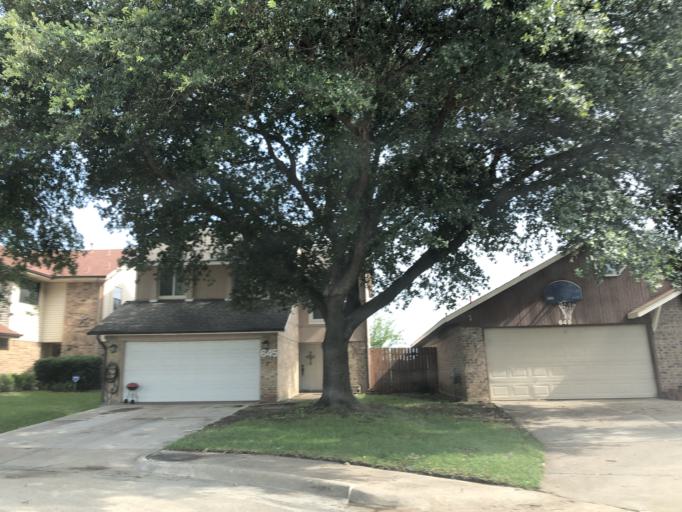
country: US
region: Texas
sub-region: Dallas County
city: Sunnyvale
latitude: 32.8330
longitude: -96.6032
